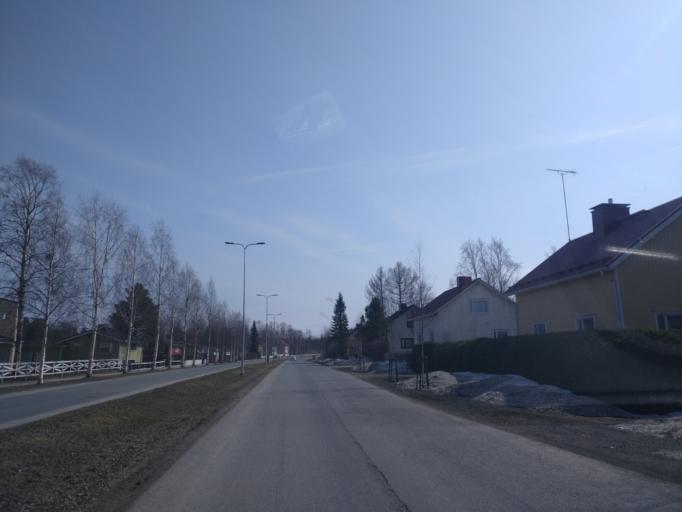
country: FI
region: Lapland
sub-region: Kemi-Tornio
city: Kemi
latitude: 65.7290
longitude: 24.6062
